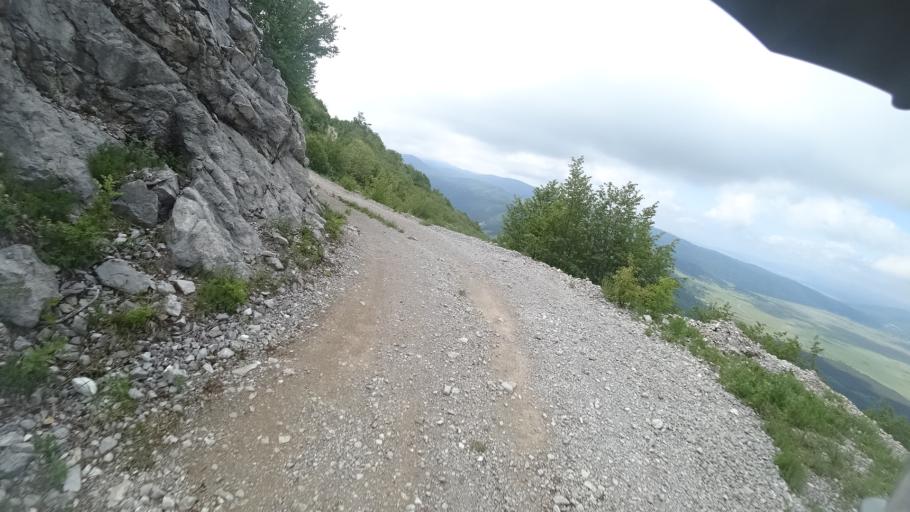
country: BA
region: Federation of Bosnia and Herzegovina
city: Bihac
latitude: 44.7082
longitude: 15.8150
